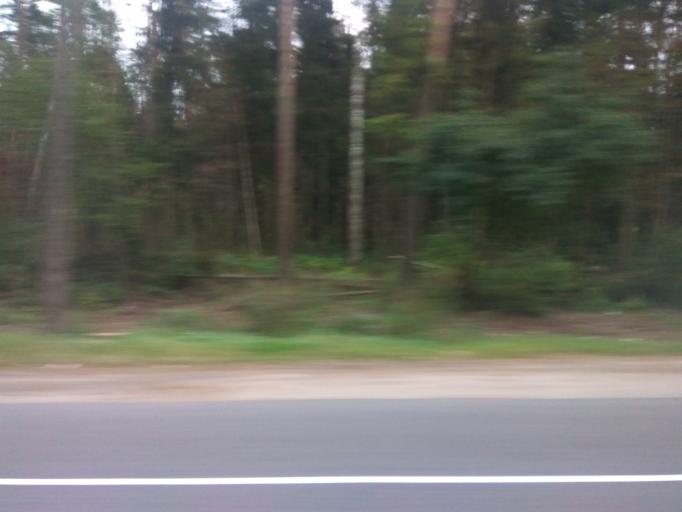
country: RU
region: Moskovskaya
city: Krasnoarmeysk
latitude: 56.0321
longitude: 38.1874
